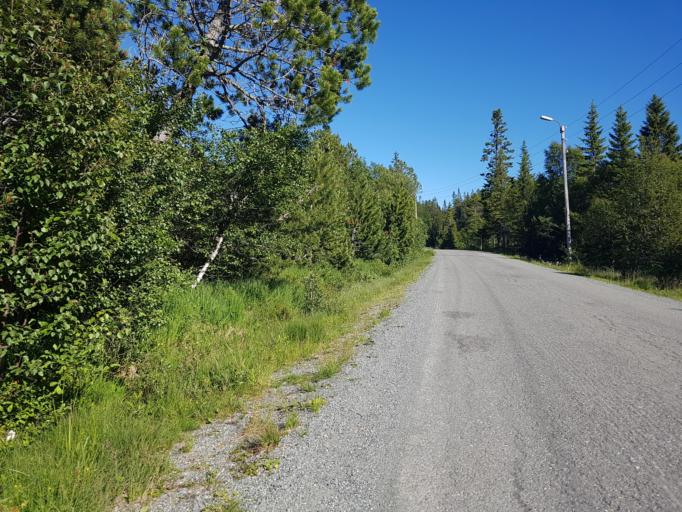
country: NO
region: Sor-Trondelag
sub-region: Trondheim
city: Trondheim
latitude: 63.4282
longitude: 10.2823
